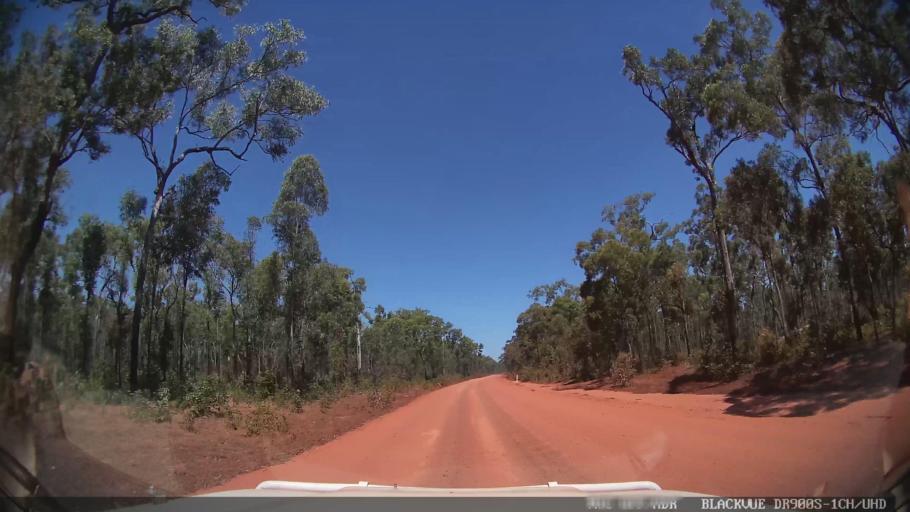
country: AU
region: Queensland
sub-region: Torres
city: Thursday Island
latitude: -11.1788
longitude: 142.2535
